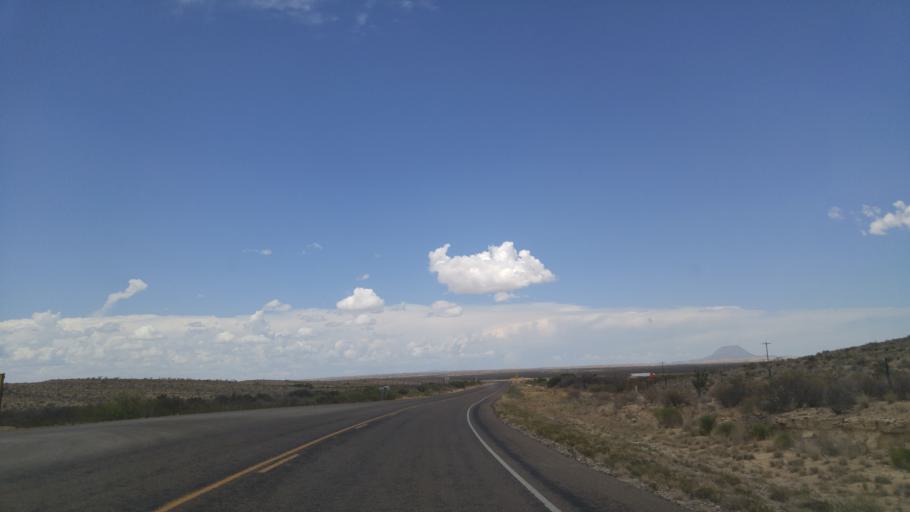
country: US
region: Texas
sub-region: Brewster County
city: Alpine
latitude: 29.5923
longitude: -103.5609
